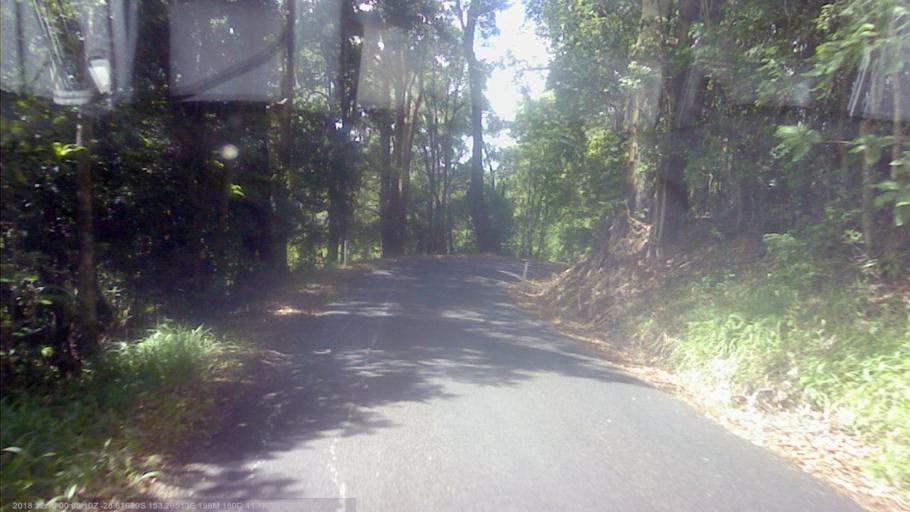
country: AU
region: New South Wales
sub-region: Lismore Municipality
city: Nimbin
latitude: -28.6169
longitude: 153.2651
